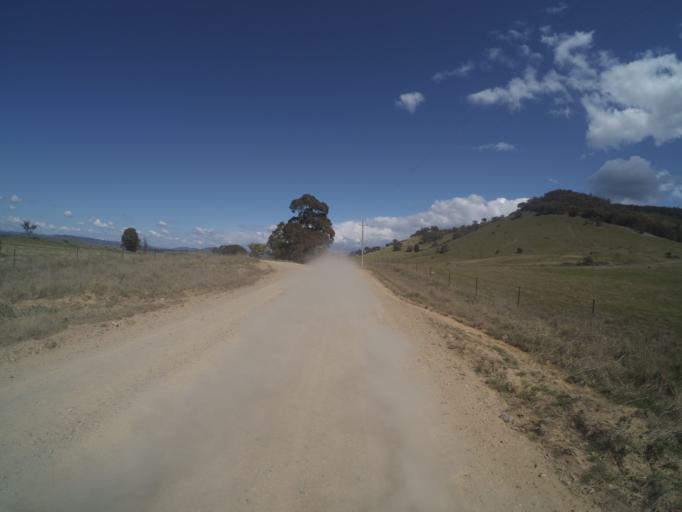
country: AU
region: Australian Capital Territory
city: Macquarie
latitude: -35.2317
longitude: 148.9124
